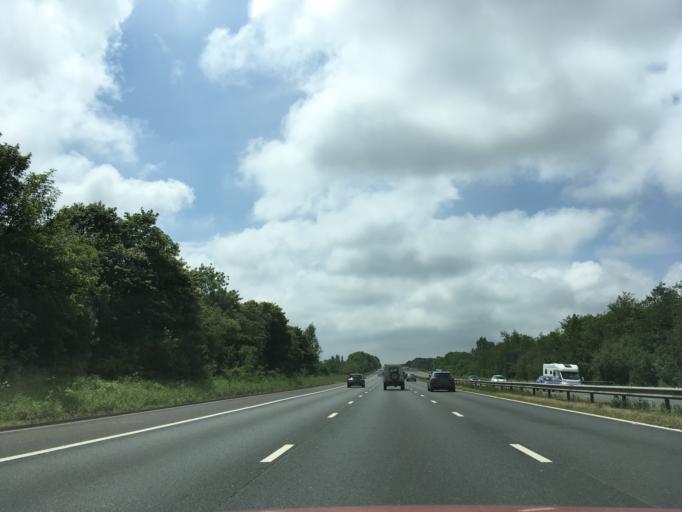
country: GB
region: England
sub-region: Devon
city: Uffculme
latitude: 50.9018
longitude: -3.3702
